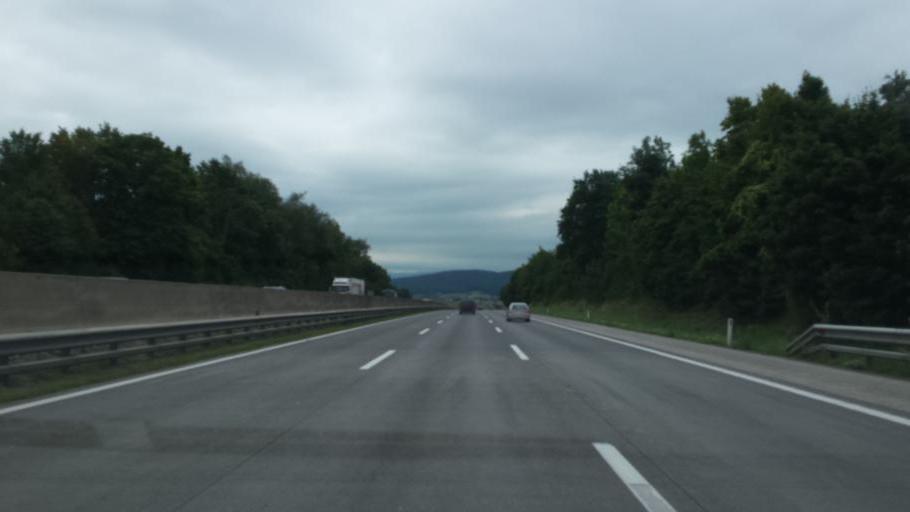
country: AT
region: Lower Austria
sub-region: Politischer Bezirk Melk
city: Melk
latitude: 48.2076
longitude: 15.3626
